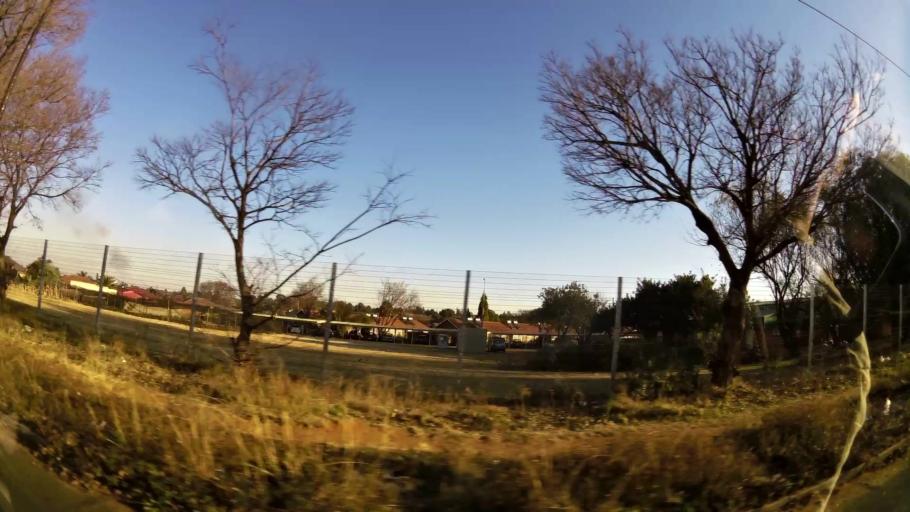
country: ZA
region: Gauteng
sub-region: City of Johannesburg Metropolitan Municipality
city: Roodepoort
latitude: -26.1621
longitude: 27.8788
